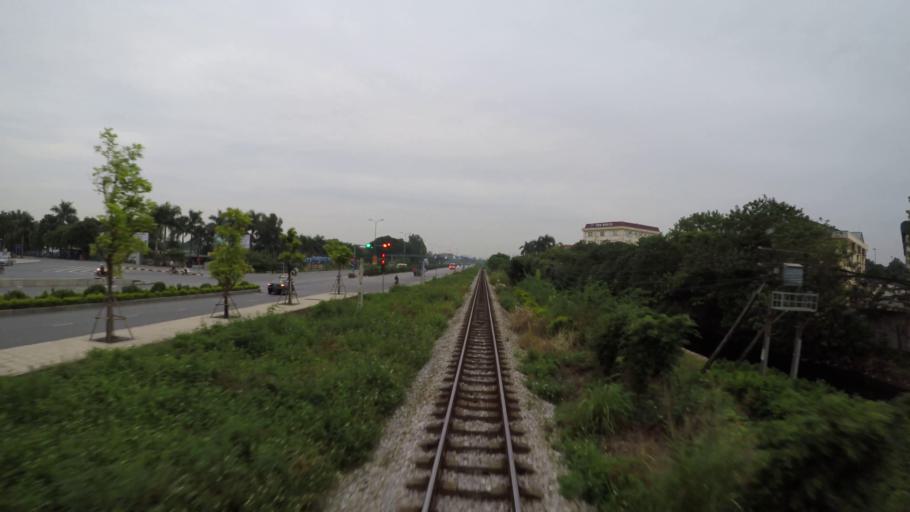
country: VN
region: Ha Noi
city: Trau Quy
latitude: 21.0146
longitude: 105.9471
